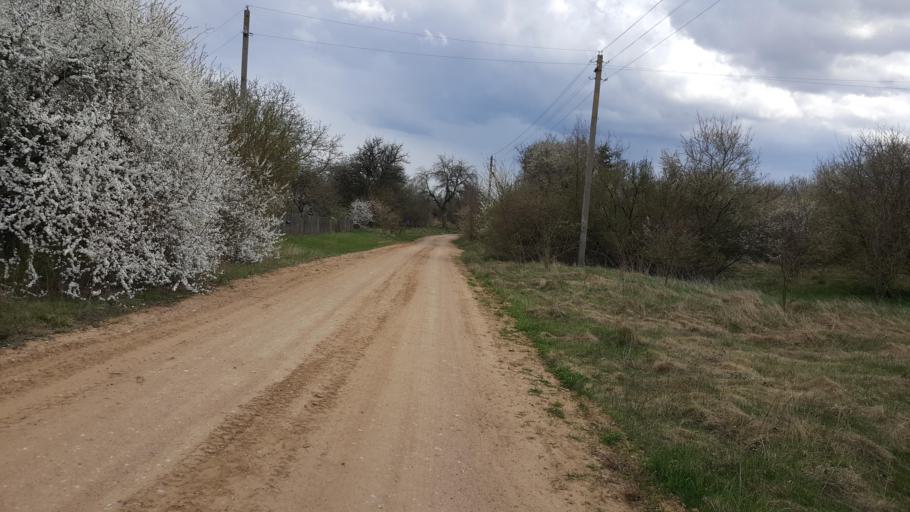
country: BY
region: Brest
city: Kamyanyets
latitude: 52.4265
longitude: 23.6996
